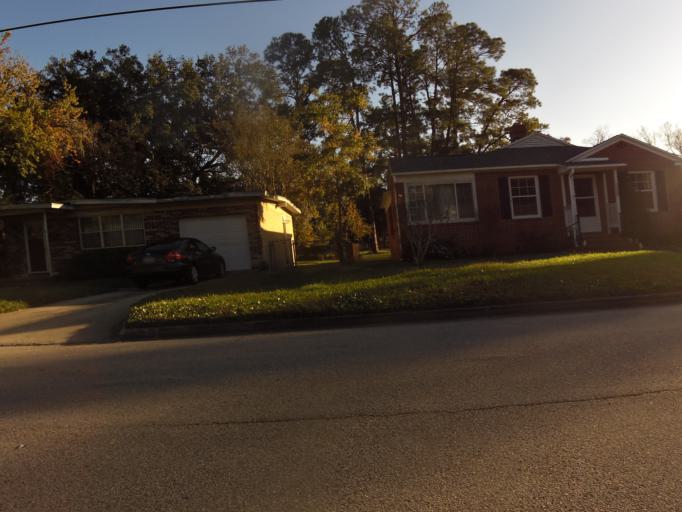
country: US
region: Florida
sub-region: Duval County
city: Jacksonville
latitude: 30.3038
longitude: -81.6398
